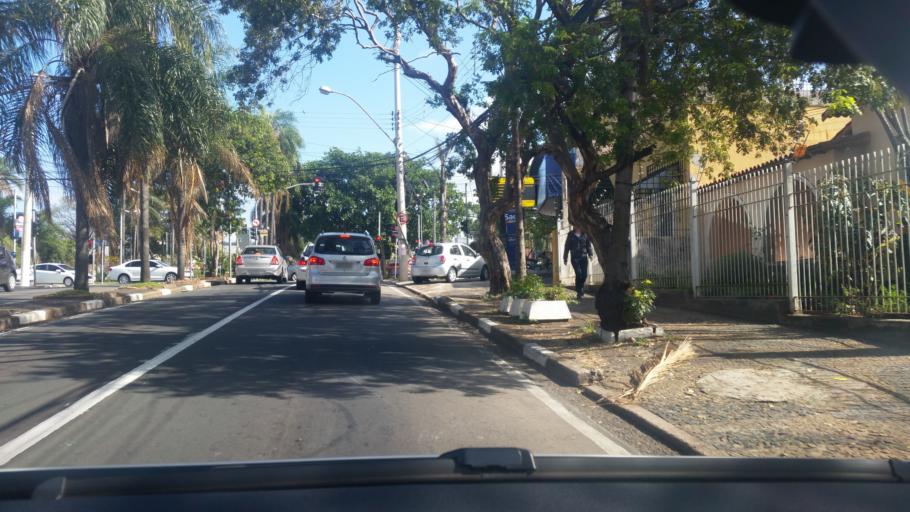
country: BR
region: Sao Paulo
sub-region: Campinas
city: Campinas
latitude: -22.8893
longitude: -47.0648
